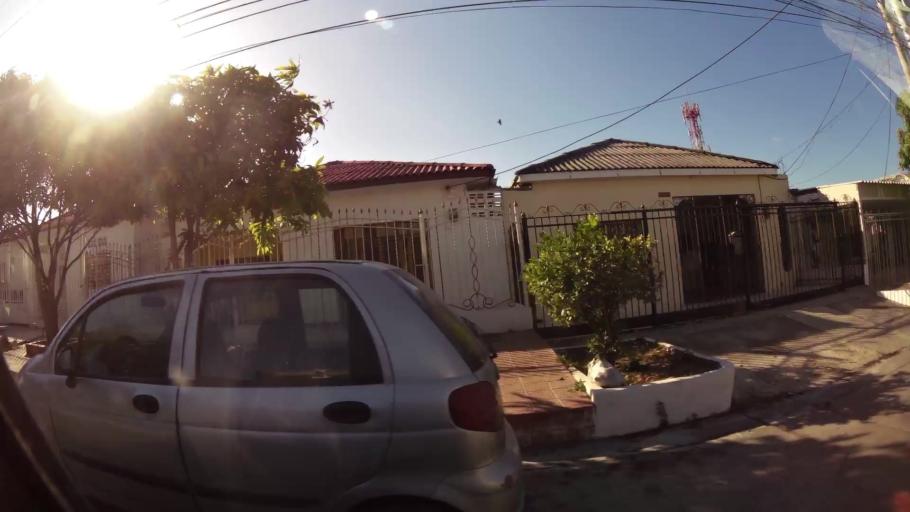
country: CO
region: Atlantico
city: Barranquilla
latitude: 10.9641
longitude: -74.7902
